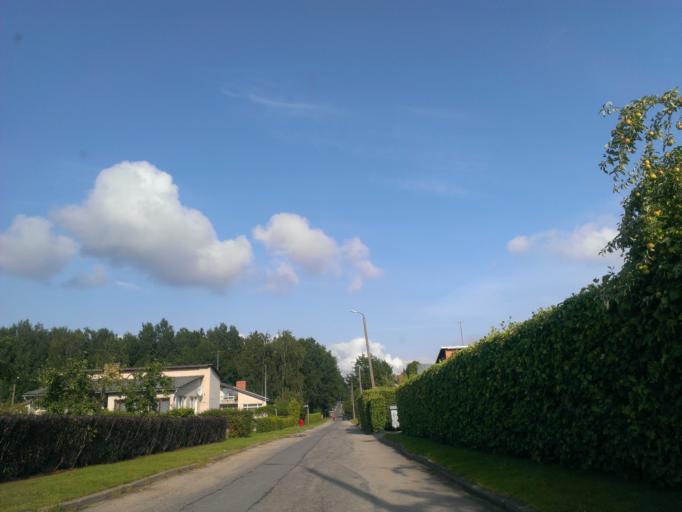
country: LV
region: Priekuli
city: Priekuli
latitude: 57.3119
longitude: 25.3414
